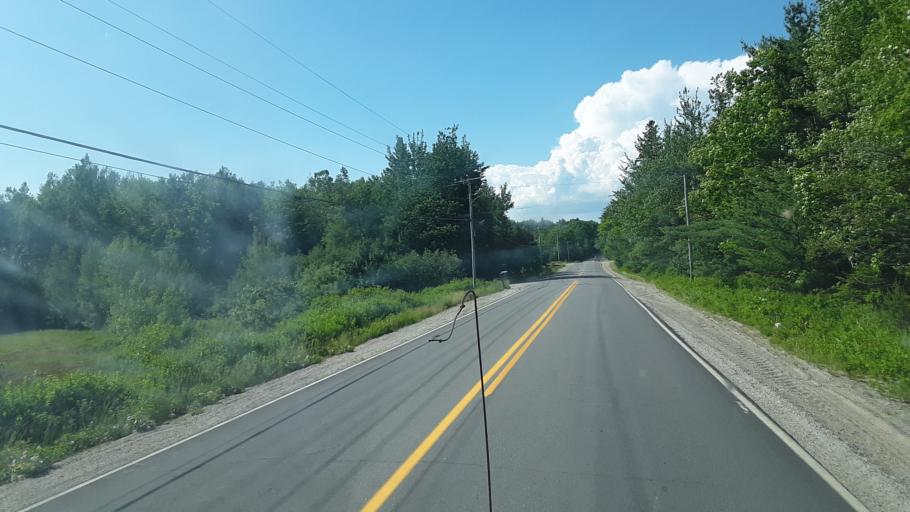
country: US
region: Maine
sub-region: Washington County
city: Cherryfield
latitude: 44.6233
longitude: -67.9368
